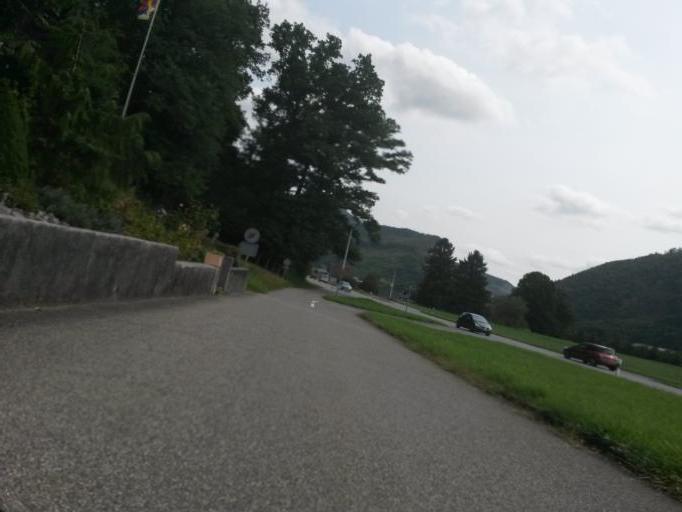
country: CH
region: Solothurn
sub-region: Bezirk Thal
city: Balsthal
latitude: 47.3124
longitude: 7.6721
